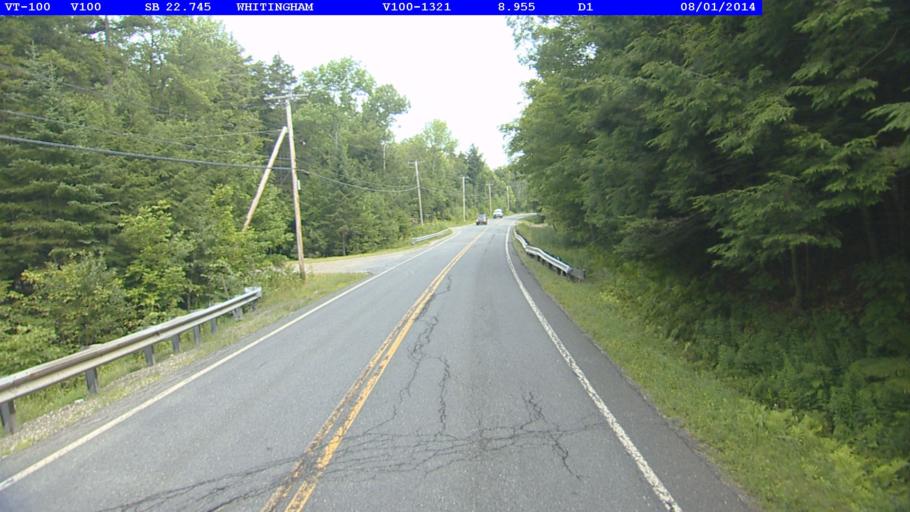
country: US
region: Vermont
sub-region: Windham County
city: Dover
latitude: 42.8091
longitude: -72.8391
